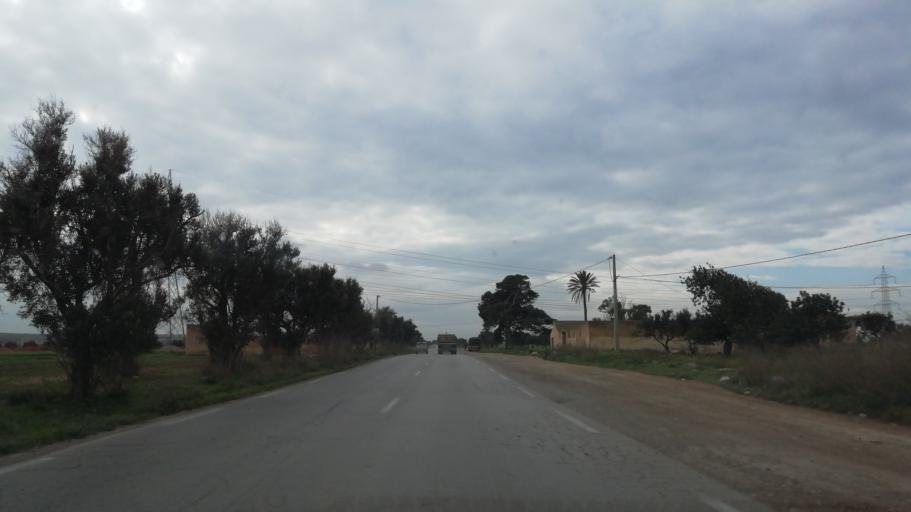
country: DZ
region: Oran
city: Ain el Bya
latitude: 35.7714
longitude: -0.3471
